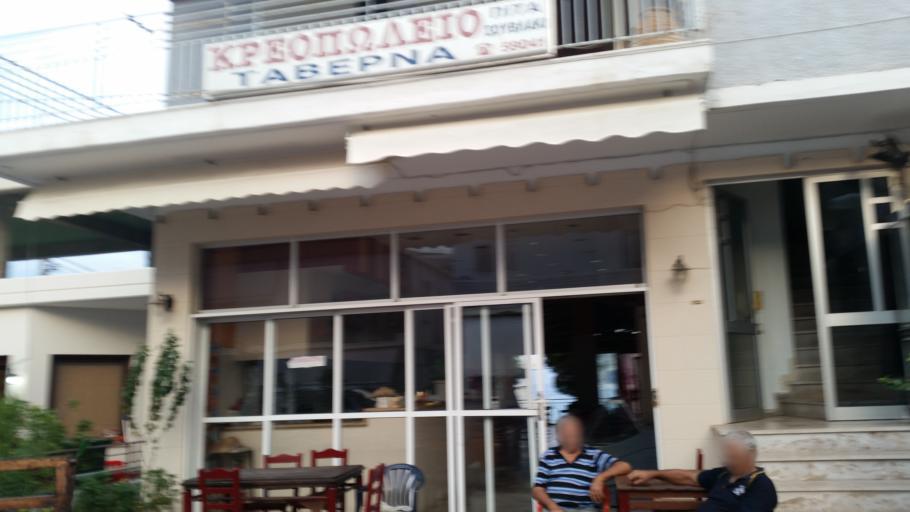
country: GR
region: Peloponnese
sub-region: Nomos Argolidos
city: Tolon
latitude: 37.5188
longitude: 22.8580
